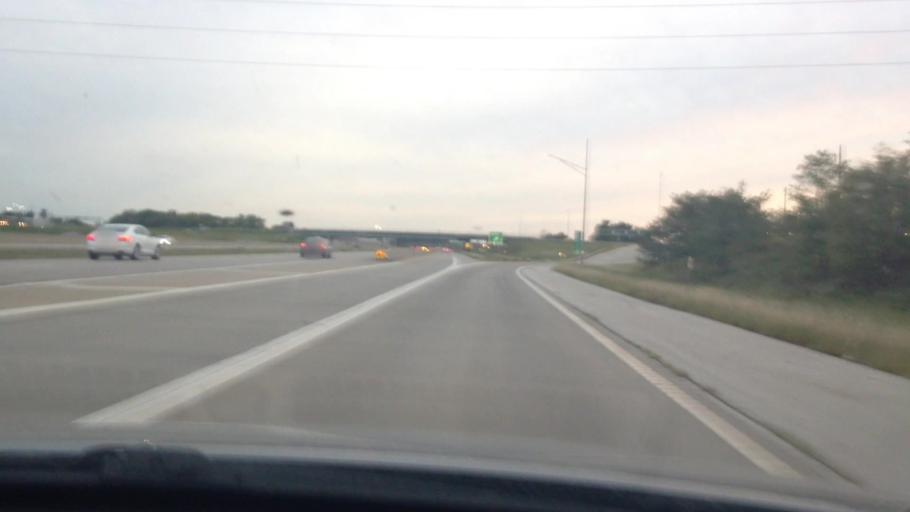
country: US
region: Missouri
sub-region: Jackson County
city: Lees Summit
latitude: 38.9377
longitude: -94.3991
